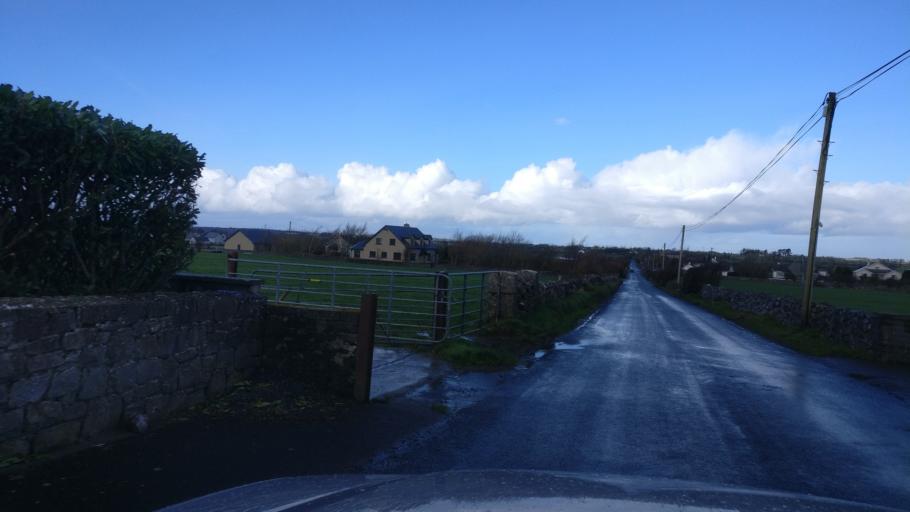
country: IE
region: Connaught
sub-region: County Galway
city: Oranmore
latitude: 53.2638
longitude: -8.8675
